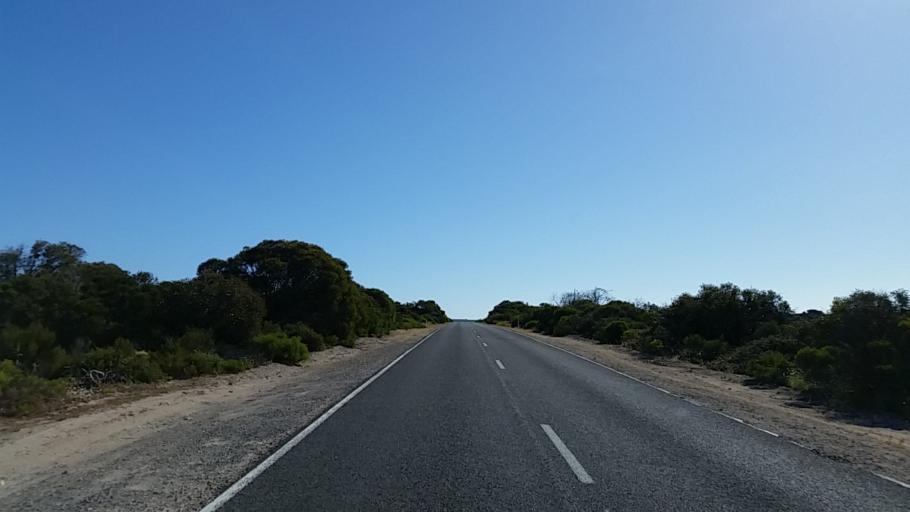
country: AU
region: South Australia
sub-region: Yorke Peninsula
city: Honiton
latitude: -35.2581
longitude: 136.9611
